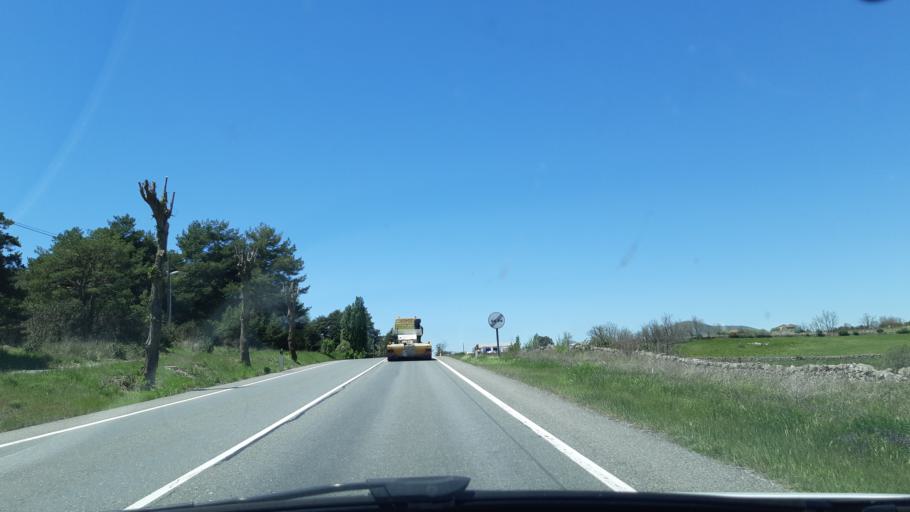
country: ES
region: Castille and Leon
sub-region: Provincia de Avila
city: Peguerinos
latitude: 40.7164
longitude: -4.2019
